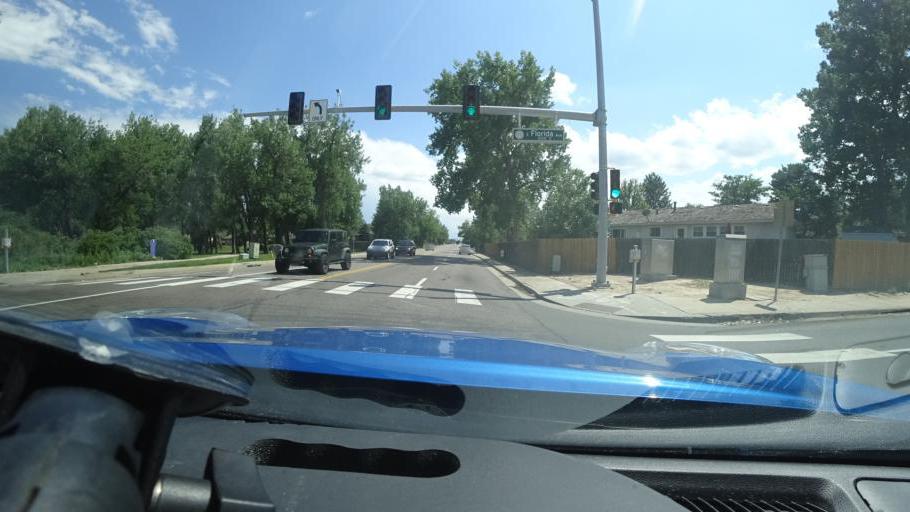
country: US
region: Colorado
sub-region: Adams County
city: Aurora
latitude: 39.6894
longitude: -104.8472
